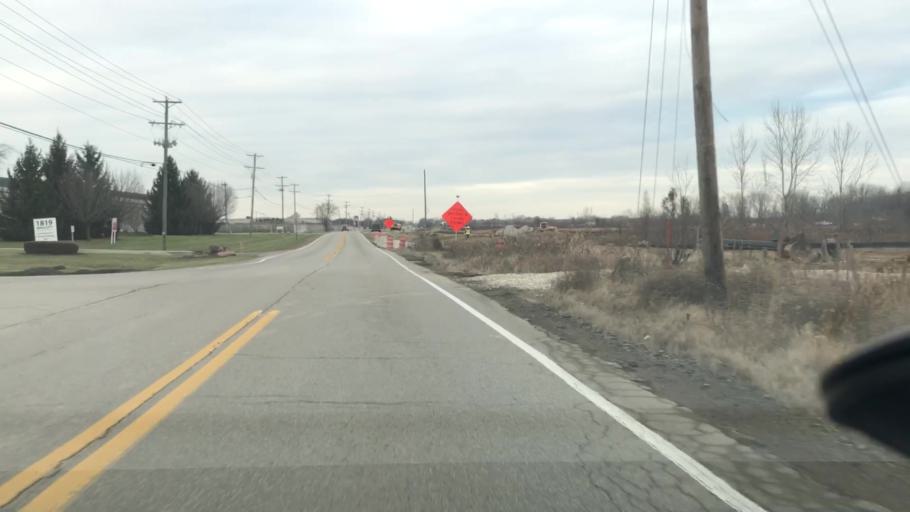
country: US
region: Ohio
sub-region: Franklin County
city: Lincoln Village
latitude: 39.9887
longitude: -83.1366
